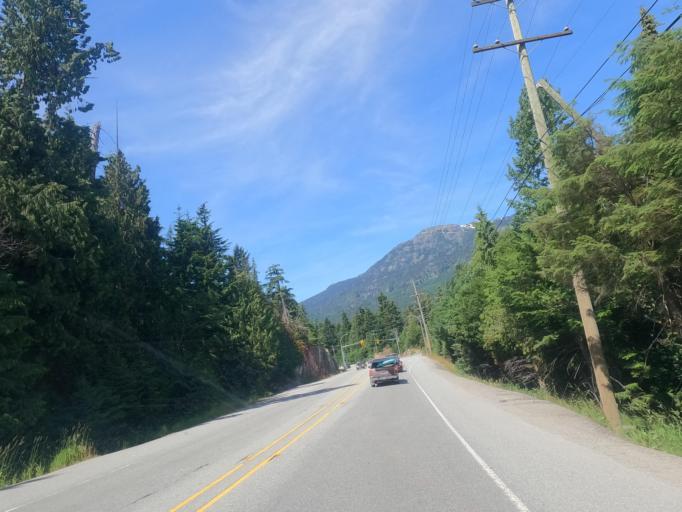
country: CA
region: British Columbia
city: Whistler
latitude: 50.1091
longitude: -122.9695
